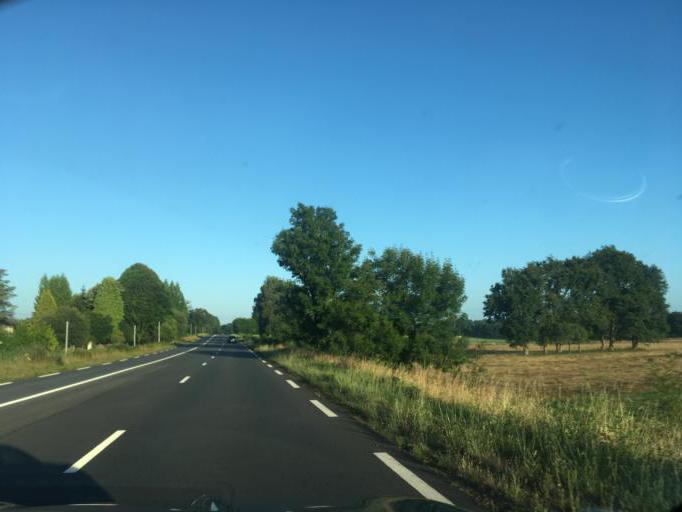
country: FR
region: Aquitaine
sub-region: Departement des Pyrenees-Atlantiques
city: Ger
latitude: 43.2481
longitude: -0.0978
